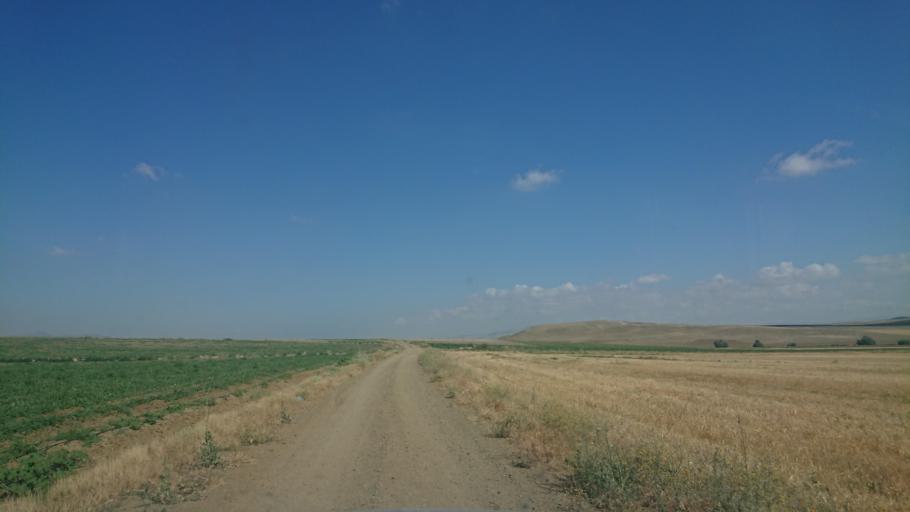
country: TR
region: Aksaray
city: Sariyahsi
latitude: 38.9648
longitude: 33.9253
